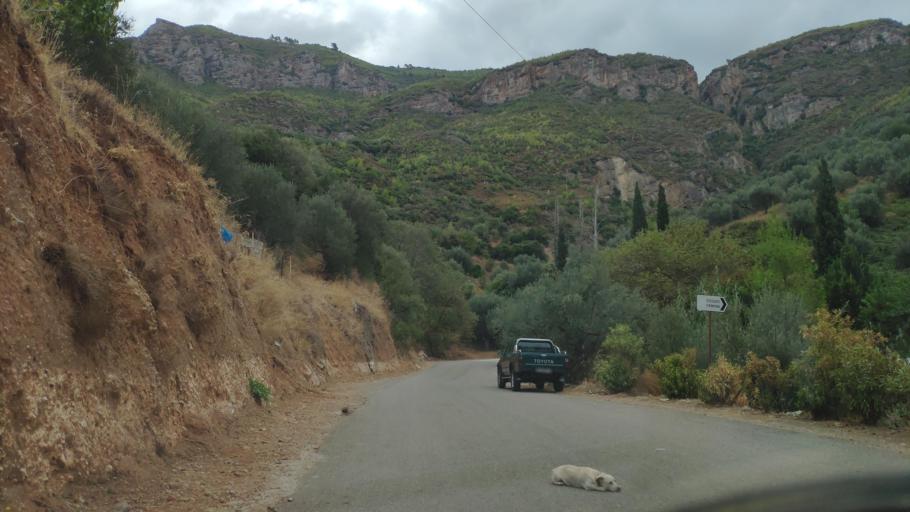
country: GR
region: West Greece
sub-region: Nomos Achaias
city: Temeni
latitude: 38.1762
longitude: 22.1441
